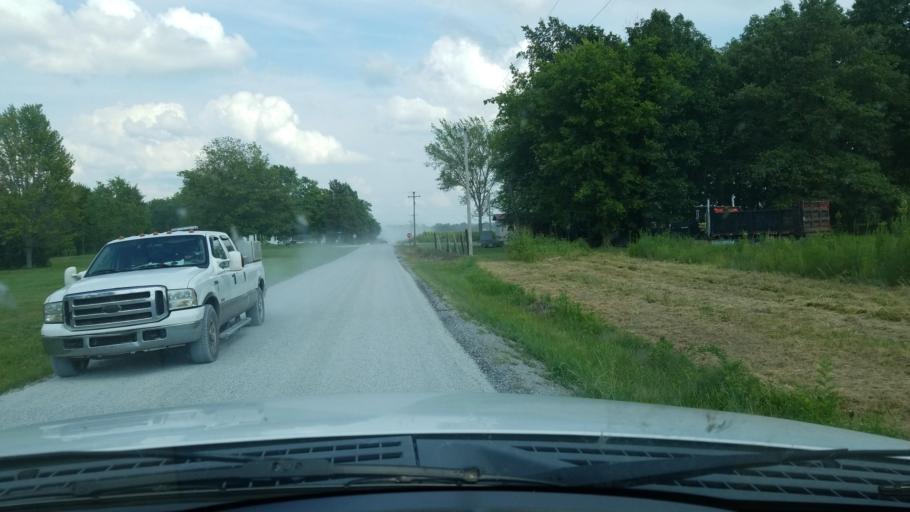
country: US
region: Illinois
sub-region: Saline County
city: Eldorado
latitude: 37.8345
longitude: -88.4334
